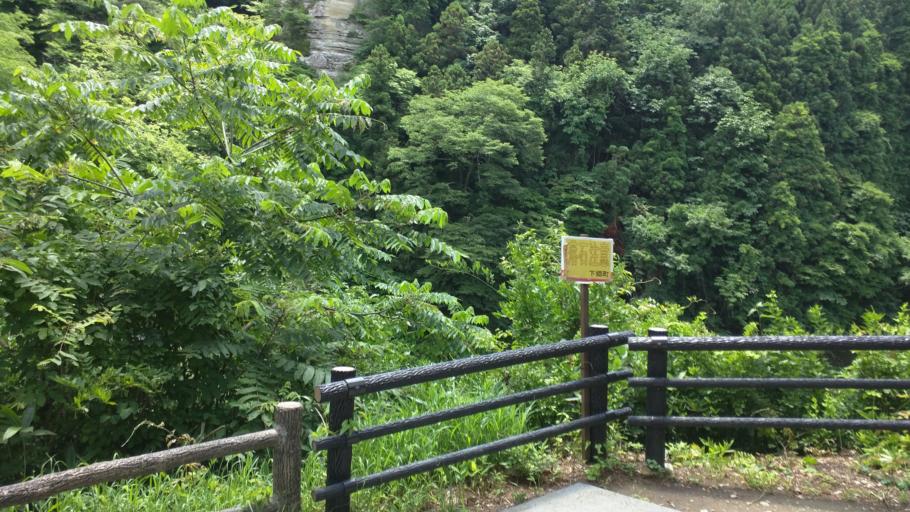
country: JP
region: Tochigi
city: Kuroiso
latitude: 37.2738
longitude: 139.9055
